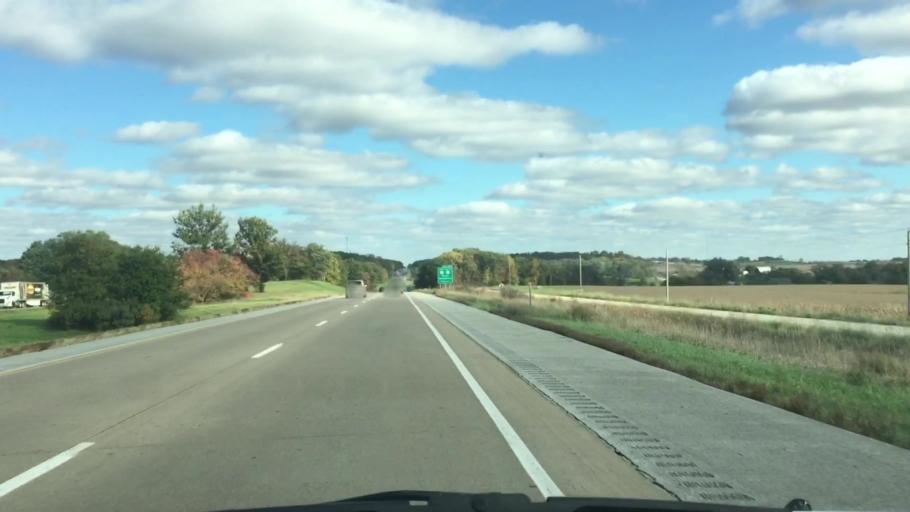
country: US
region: Iowa
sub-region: Muscatine County
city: Wilton
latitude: 41.6429
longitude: -91.0707
